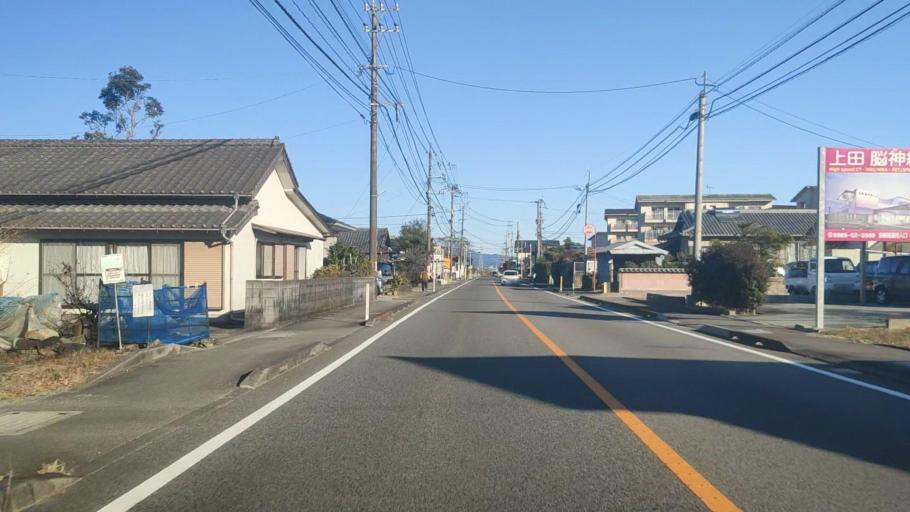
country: JP
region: Miyazaki
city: Nobeoka
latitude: 32.3838
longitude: 131.6275
